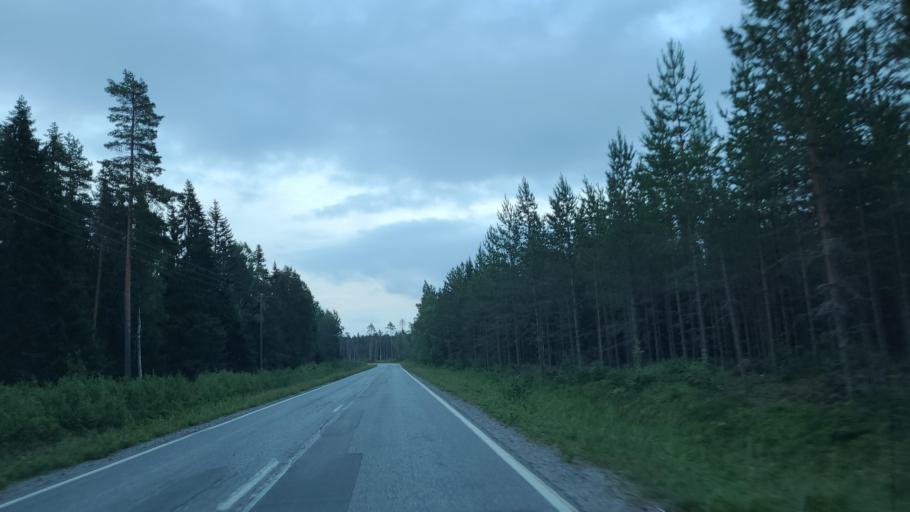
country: FI
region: Ostrobothnia
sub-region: Vaasa
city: Replot
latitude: 63.2055
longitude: 21.2665
